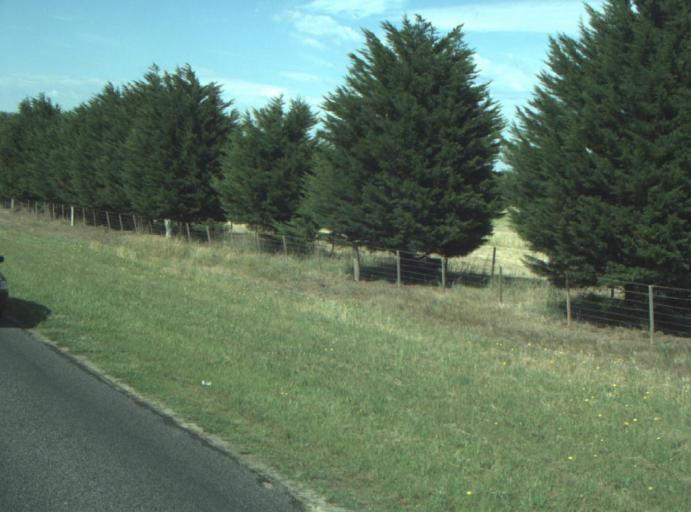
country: AU
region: Victoria
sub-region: Greater Geelong
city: Leopold
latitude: -38.2015
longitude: 144.5091
